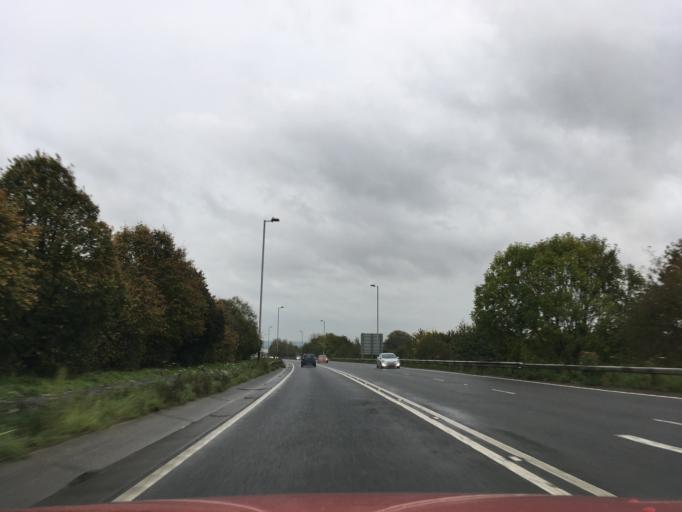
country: GB
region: Wales
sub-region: Monmouthshire
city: Chepstow
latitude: 51.6326
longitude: -2.6843
